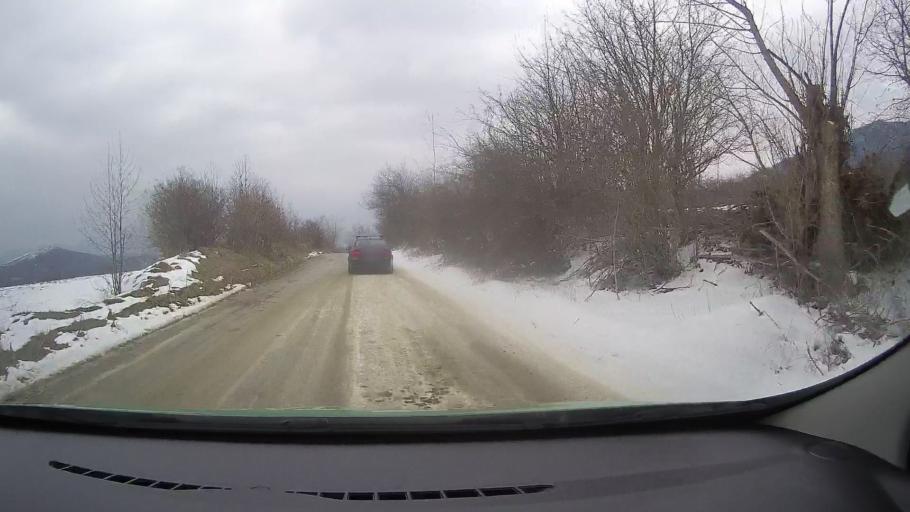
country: RO
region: Brasov
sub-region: Comuna Zarnesti
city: Zarnesti
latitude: 45.5425
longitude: 25.3261
